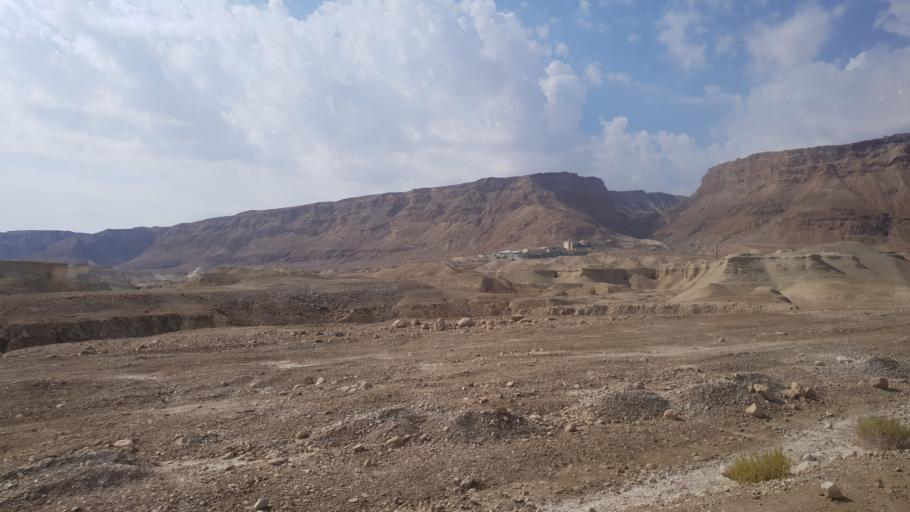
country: IL
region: Southern District
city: `En Boqeq
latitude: 31.3172
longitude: 35.3775
